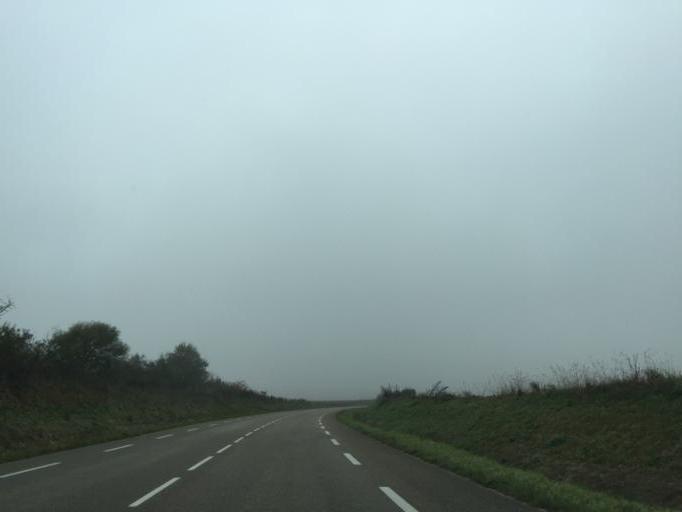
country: FR
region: Rhone-Alpes
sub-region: Departement de l'Ain
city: Chazey-sur-Ain
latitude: 45.8559
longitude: 5.2555
